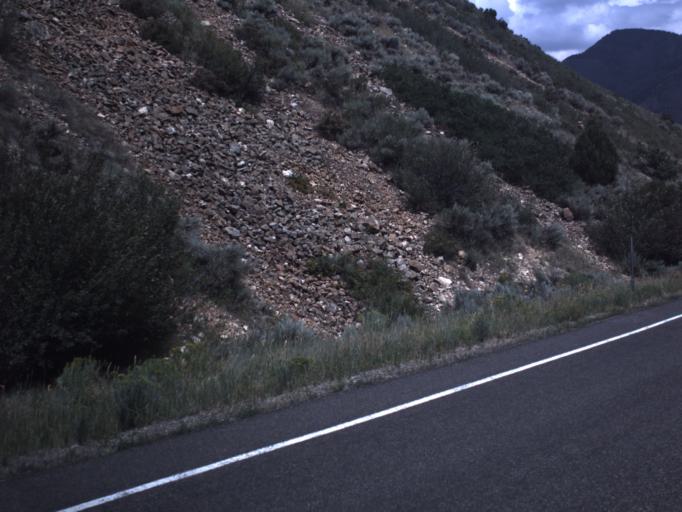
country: US
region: Utah
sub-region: Summit County
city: Francis
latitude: 40.4591
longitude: -110.8477
